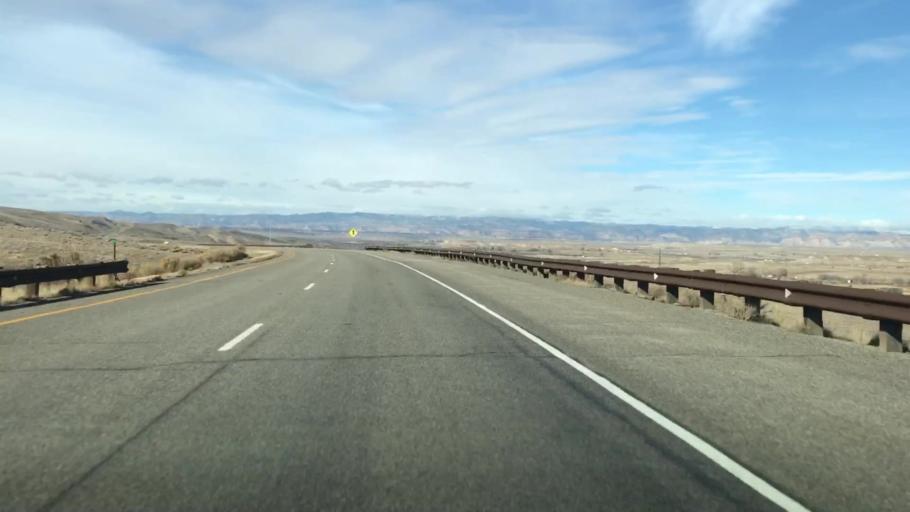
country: US
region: Colorado
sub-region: Mesa County
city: Loma
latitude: 39.2148
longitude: -108.8683
